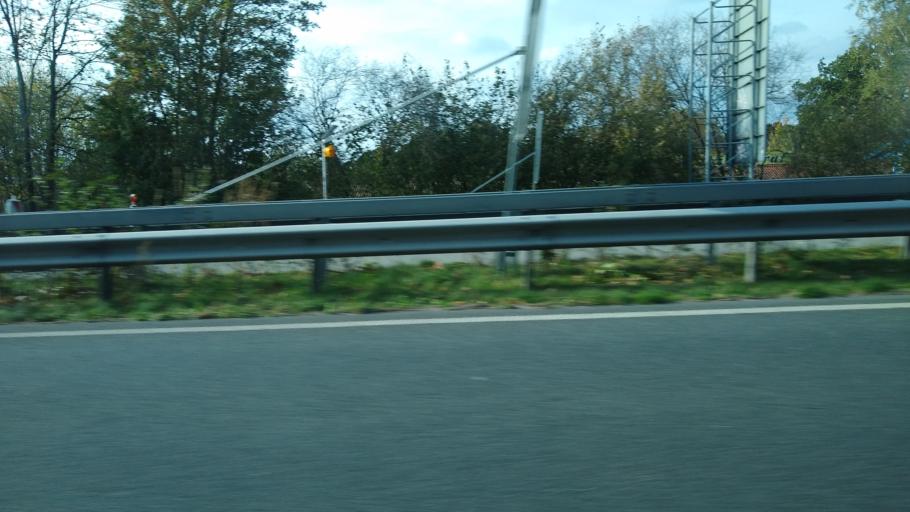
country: DE
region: Lower Saxony
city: Oldenburg
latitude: 53.1776
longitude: 8.2259
